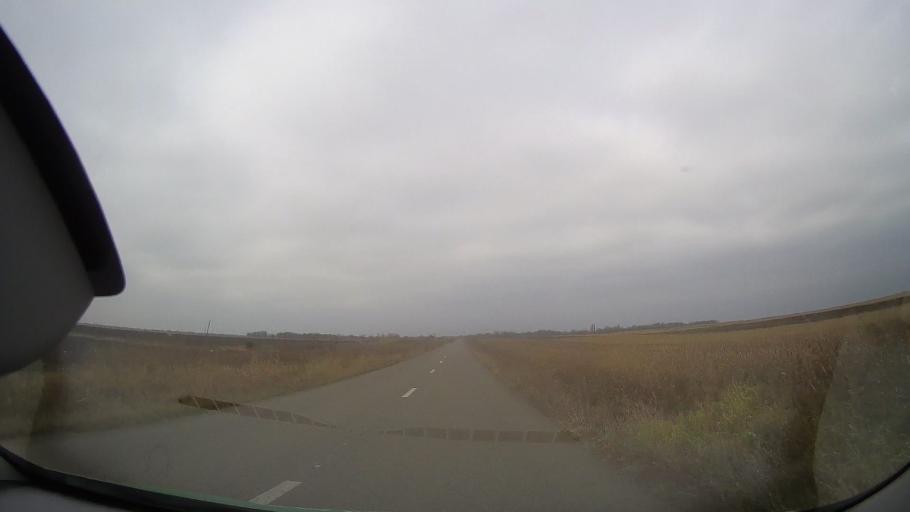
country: RO
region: Buzau
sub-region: Comuna Scutelnici
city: Scutelnici
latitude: 44.8668
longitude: 26.8931
